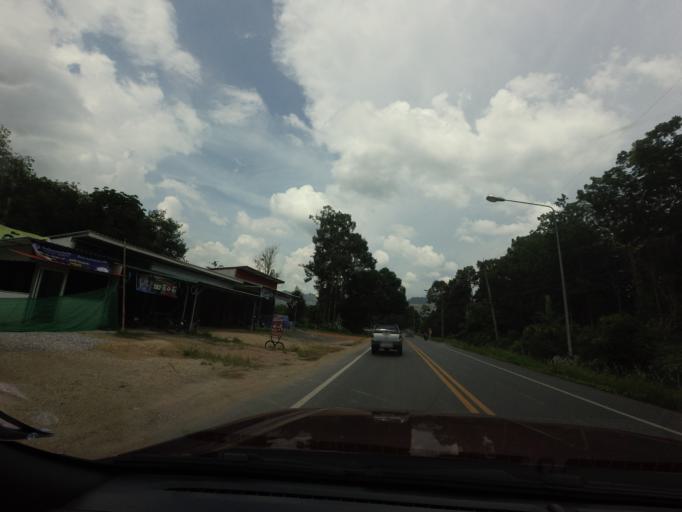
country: TH
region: Yala
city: Ban Nang Sata
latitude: 6.2643
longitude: 101.2741
